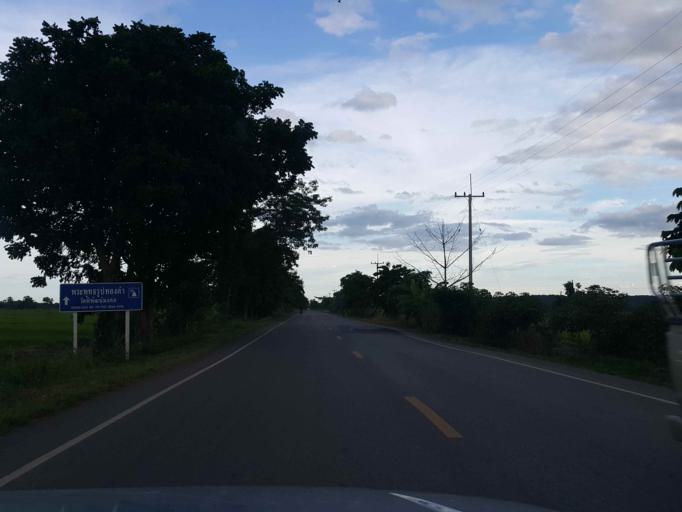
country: TH
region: Sukhothai
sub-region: Amphoe Si Satchanalai
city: Si Satchanalai
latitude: 17.4197
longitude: 99.7261
